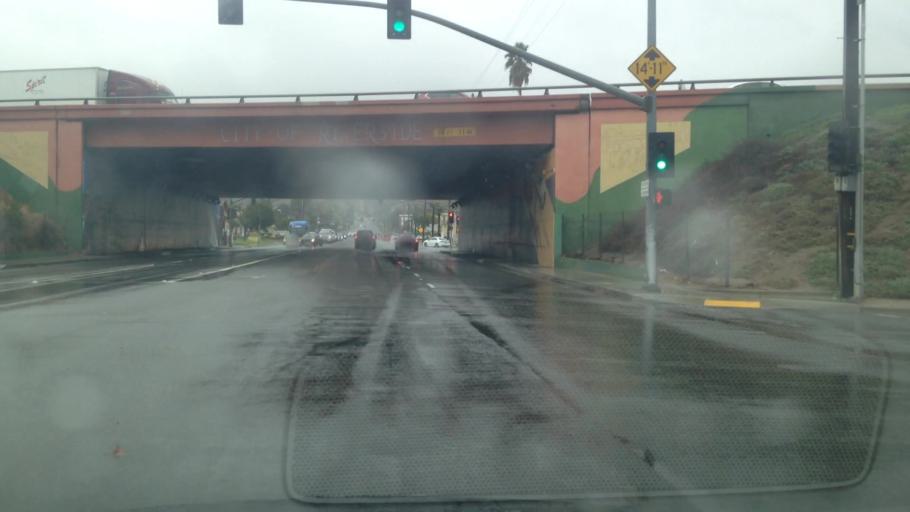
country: US
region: California
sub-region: Riverside County
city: Home Gardens
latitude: 33.8978
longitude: -117.4934
